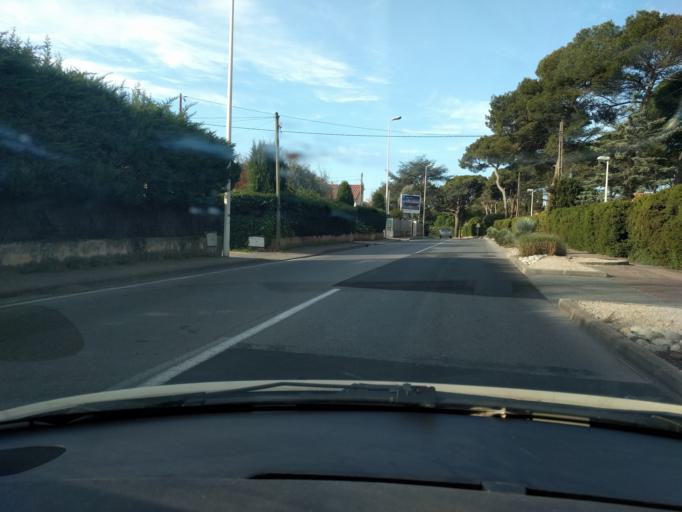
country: FR
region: Provence-Alpes-Cote d'Azur
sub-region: Departement des Alpes-Maritimes
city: Mougins
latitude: 43.5729
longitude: 6.9838
